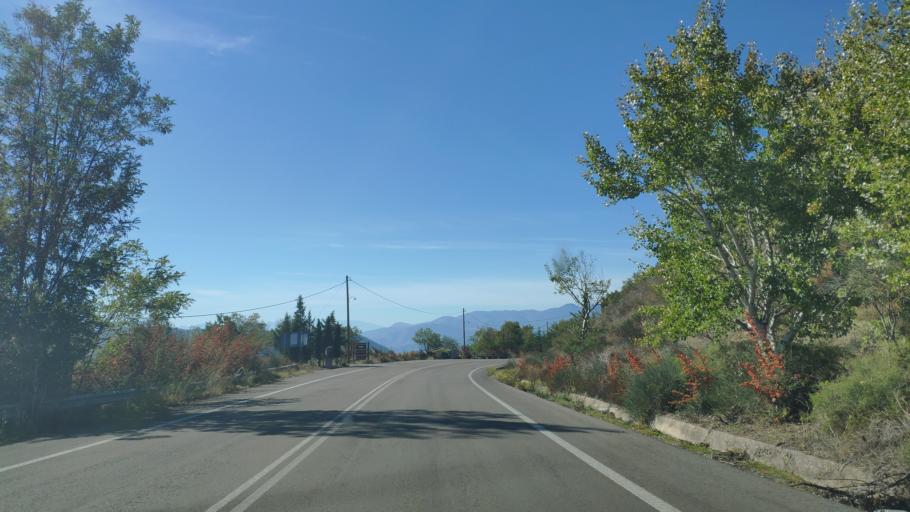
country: GR
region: Central Greece
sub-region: Nomos Voiotias
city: Arachova
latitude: 38.4857
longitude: 22.5681
